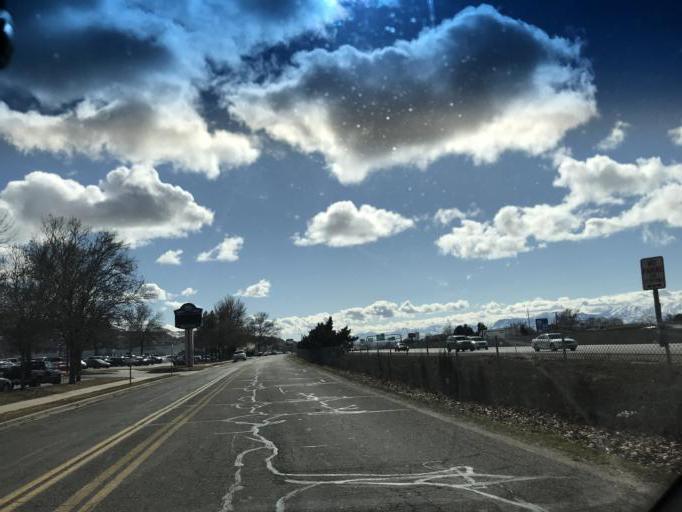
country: US
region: Utah
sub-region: Davis County
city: Woods Cross
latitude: 40.8691
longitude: -111.8971
